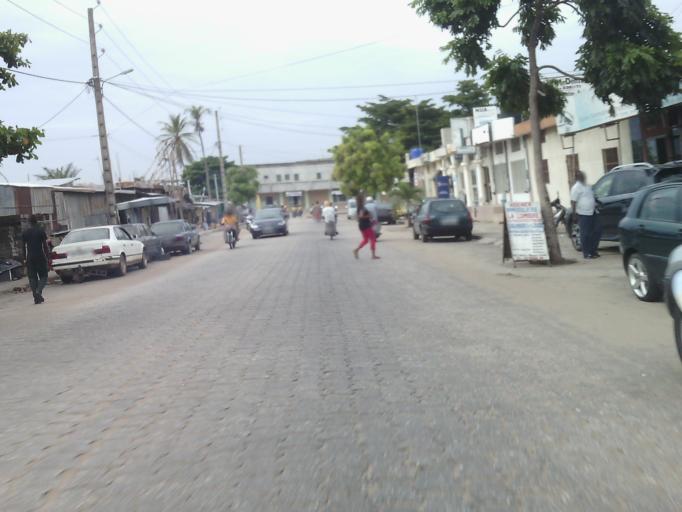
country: BJ
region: Littoral
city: Cotonou
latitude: 6.3884
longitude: 2.3762
